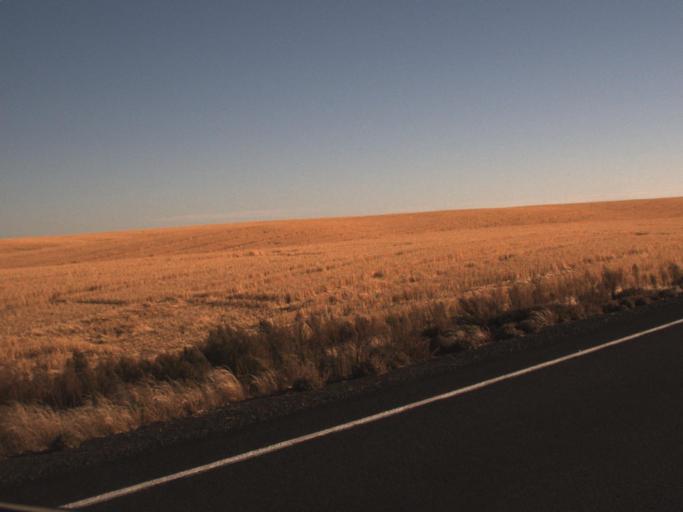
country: US
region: Washington
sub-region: Adams County
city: Ritzville
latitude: 46.8980
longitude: -118.3333
